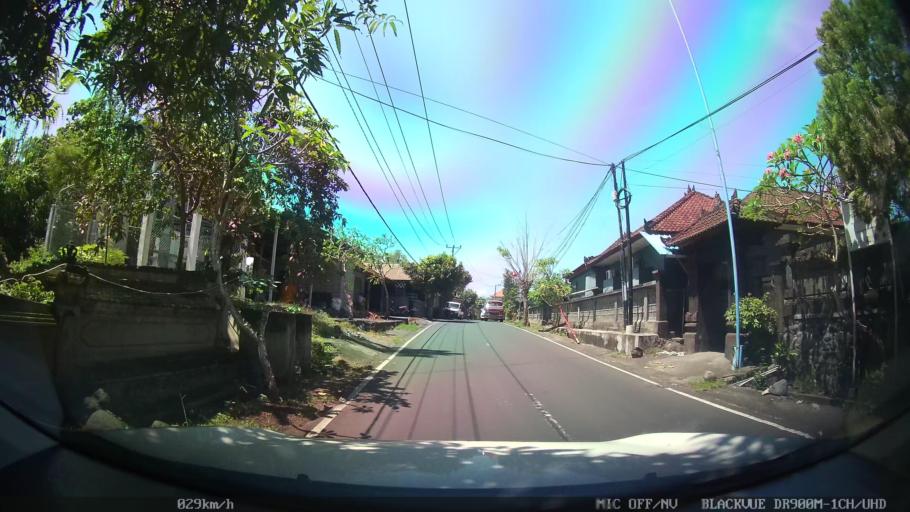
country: ID
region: Bali
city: Klungkung
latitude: -8.5709
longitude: 115.3338
